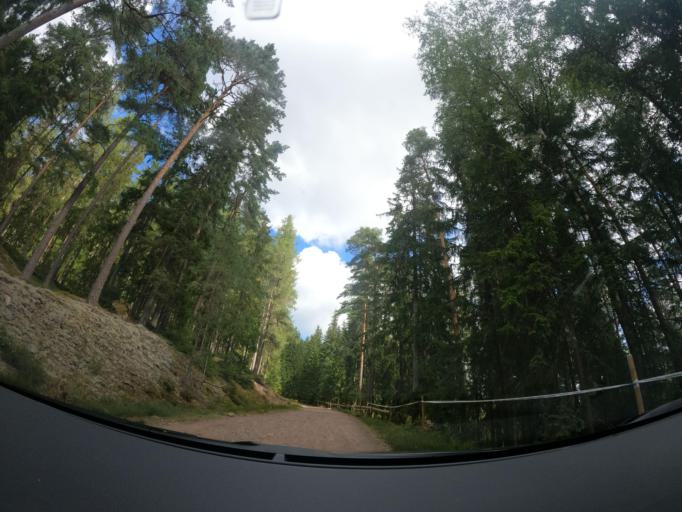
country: SE
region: Joenkoeping
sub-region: Gislaveds Kommun
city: Gislaved
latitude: 57.4278
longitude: 13.6112
